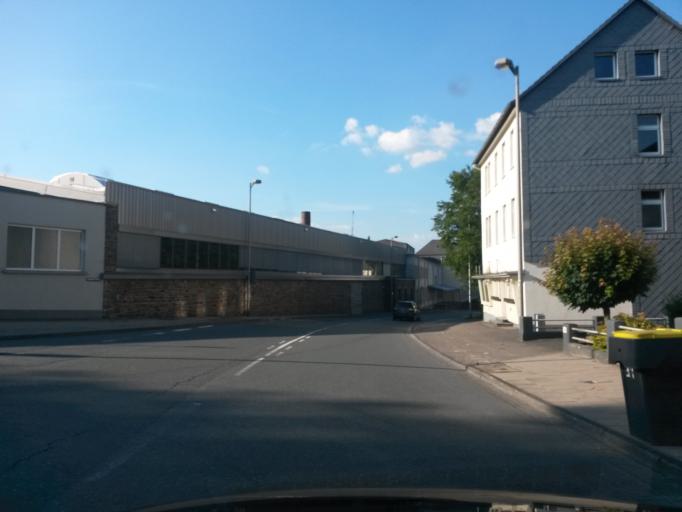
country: DE
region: North Rhine-Westphalia
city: Meinerzhagen
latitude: 51.1034
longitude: 7.6374
